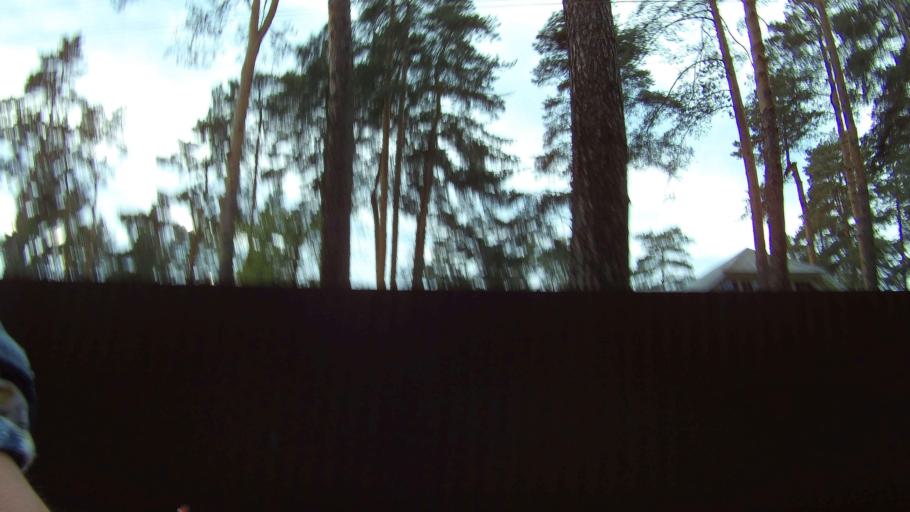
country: RU
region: Moskovskaya
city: Kratovo
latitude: 55.5840
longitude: 38.1861
